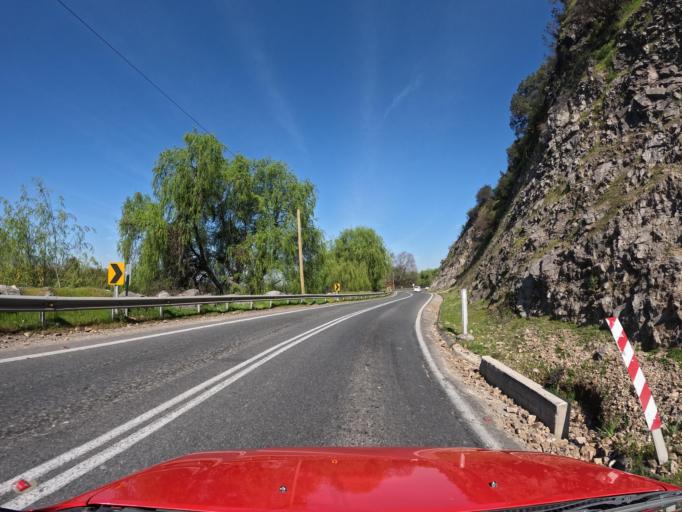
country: CL
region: Maule
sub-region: Provincia de Curico
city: Rauco
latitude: -34.9875
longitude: -71.4264
